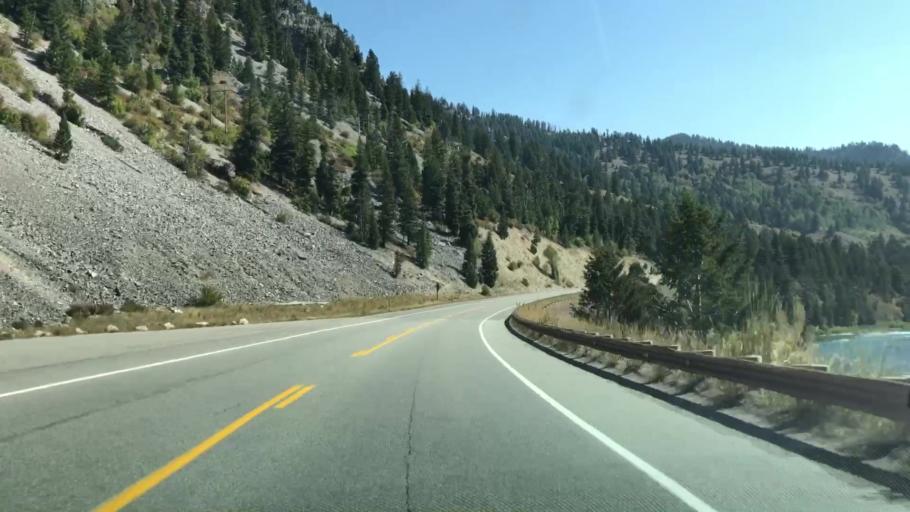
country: US
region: Wyoming
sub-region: Teton County
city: Hoback
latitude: 43.1970
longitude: -110.9089
